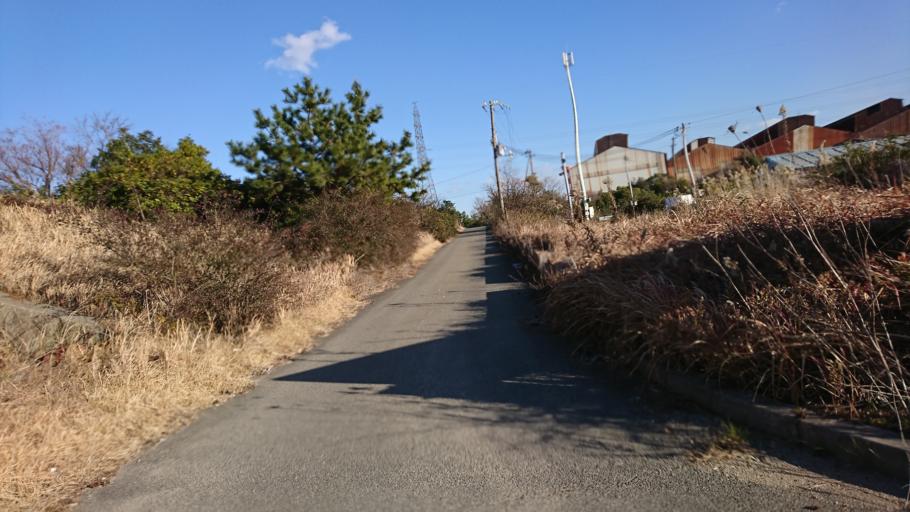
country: JP
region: Hyogo
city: Kakogawacho-honmachi
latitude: 34.7294
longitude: 134.8197
